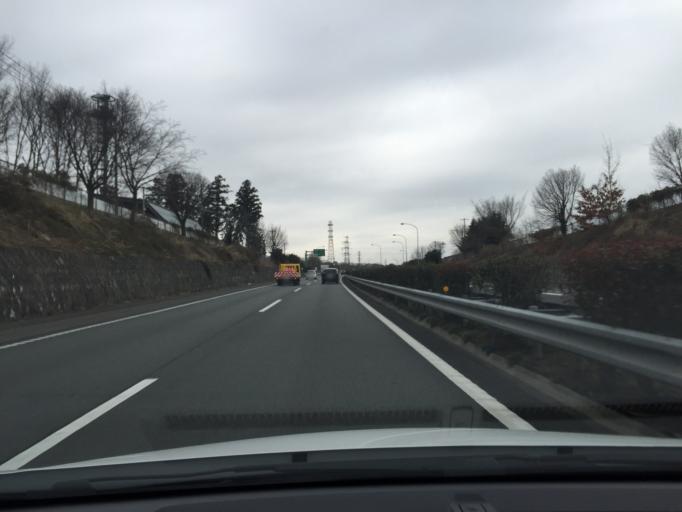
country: JP
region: Saitama
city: Hanno
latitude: 35.7991
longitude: 139.3268
